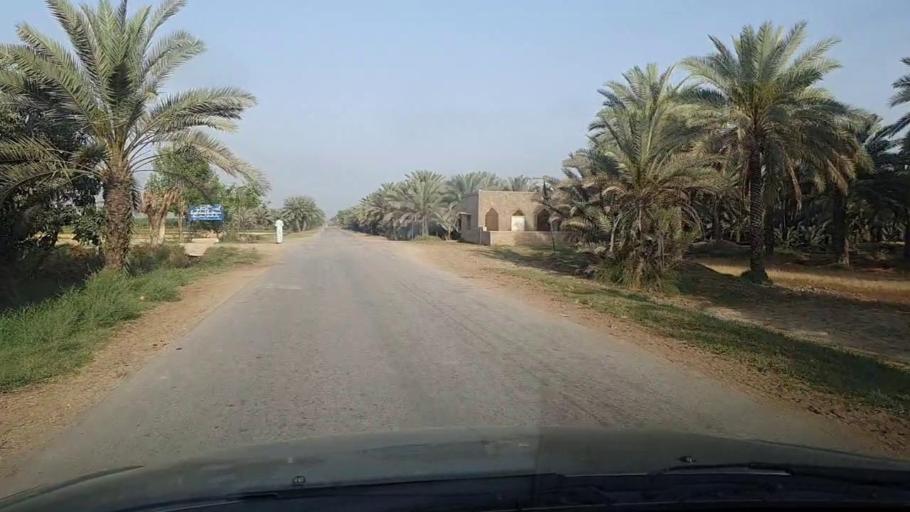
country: PK
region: Sindh
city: Pir jo Goth
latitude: 27.5638
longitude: 68.6516
